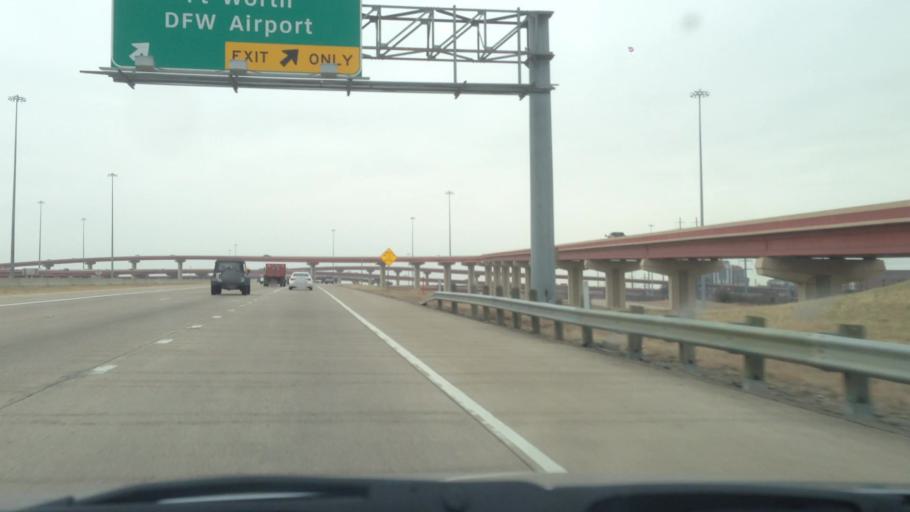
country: US
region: Texas
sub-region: Tarrant County
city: Euless
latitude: 32.8435
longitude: -97.0171
